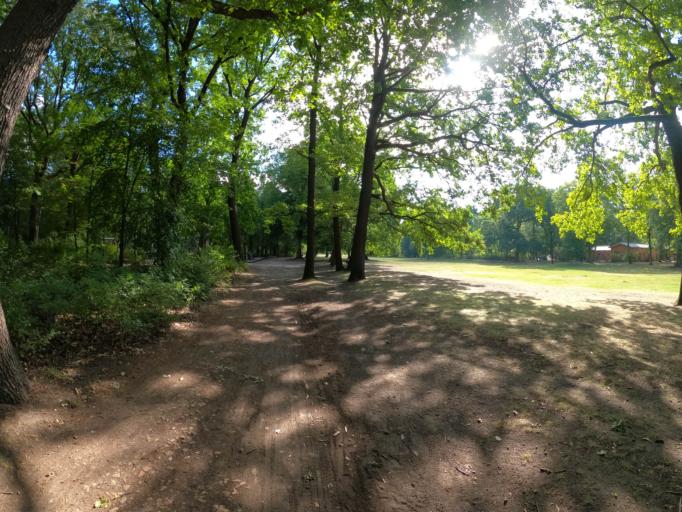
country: DE
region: Berlin
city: Charlottenburg-Nord
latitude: 52.5442
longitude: 13.2851
